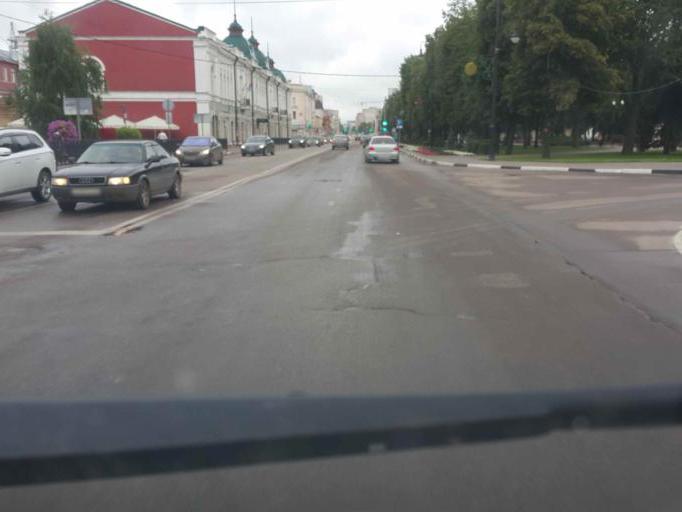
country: RU
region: Tambov
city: Tambov
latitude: 52.7215
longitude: 41.4518
